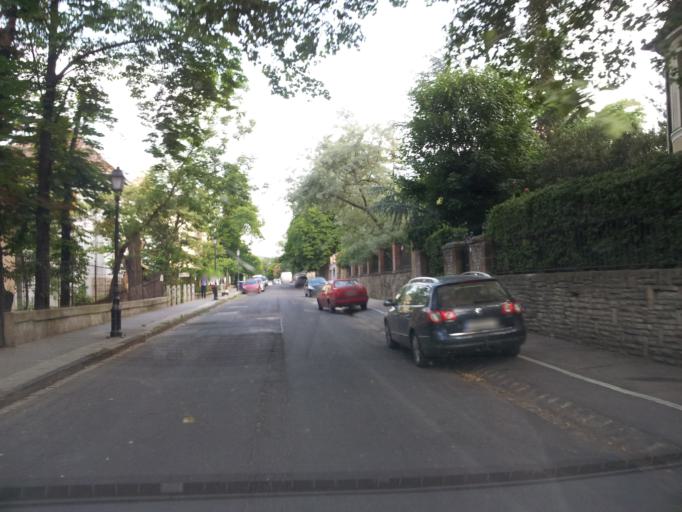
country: HU
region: Budapest
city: Budapest I. keruelet
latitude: 47.4910
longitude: 19.0344
